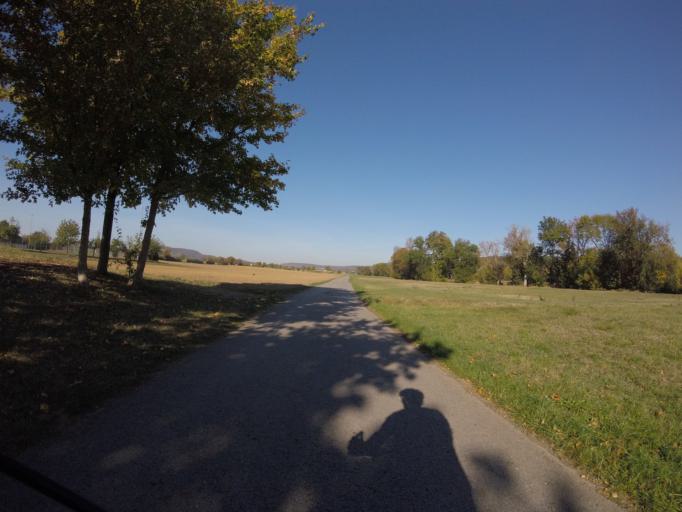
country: DE
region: Baden-Wuerttemberg
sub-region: Regierungsbezirk Stuttgart
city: Sersheim
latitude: 48.9660
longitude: 9.0067
